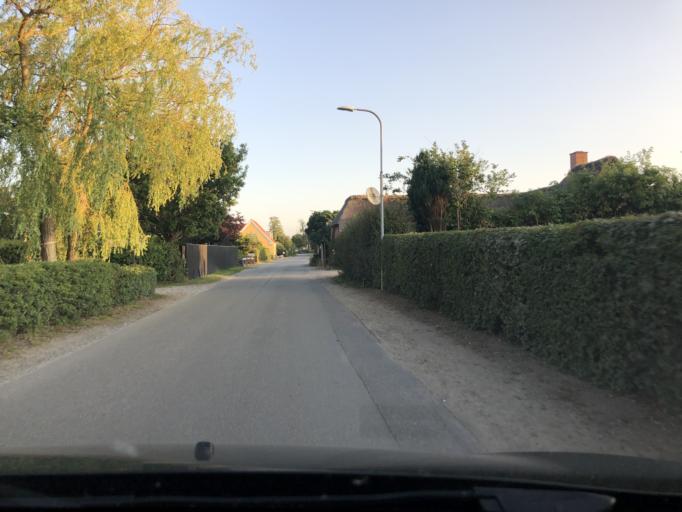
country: DK
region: South Denmark
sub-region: Fredericia Kommune
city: Fredericia
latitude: 55.6335
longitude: 9.7416
